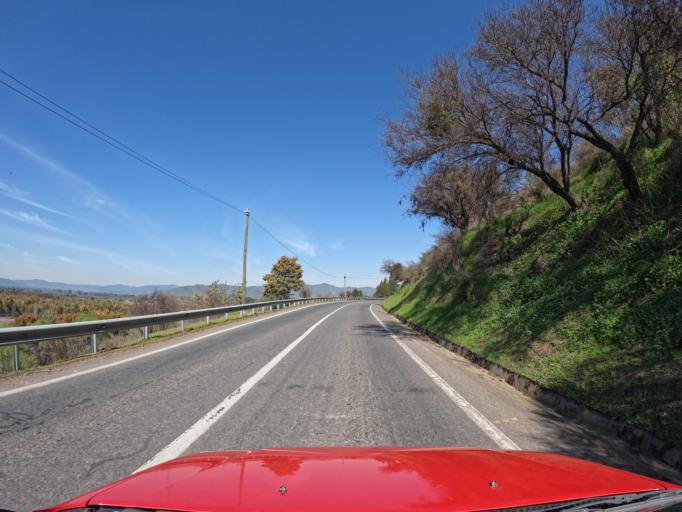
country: CL
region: Maule
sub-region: Provincia de Talca
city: Talca
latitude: -35.0865
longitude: -71.6444
